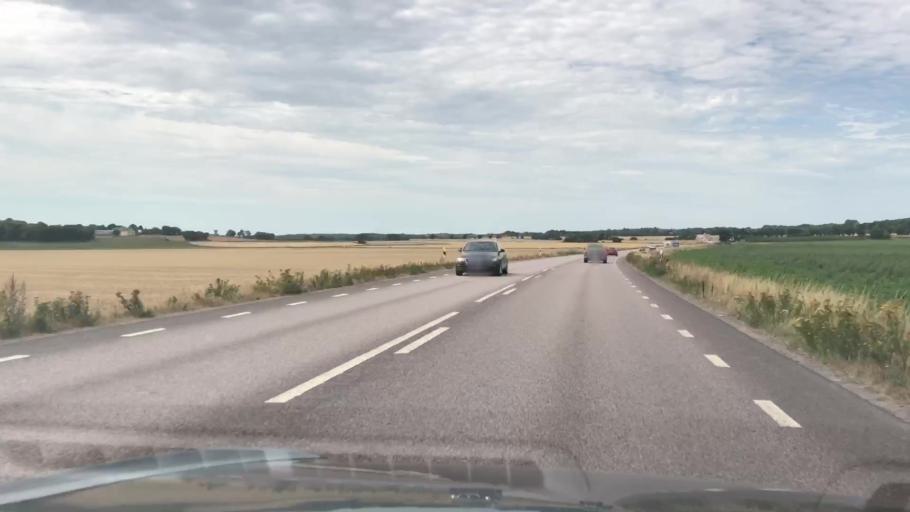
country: SE
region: Blekinge
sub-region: Karlskrona Kommun
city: Jaemjoe
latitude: 56.1845
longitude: 15.7577
